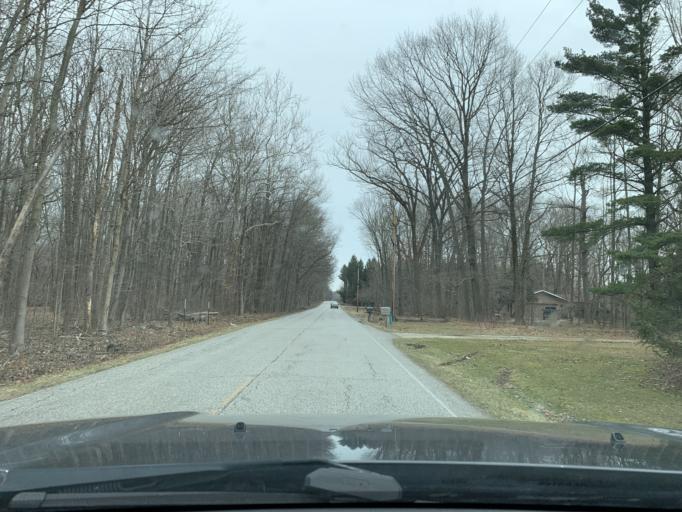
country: US
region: Indiana
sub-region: Porter County
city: Chesterton
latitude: 41.5858
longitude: -87.0046
